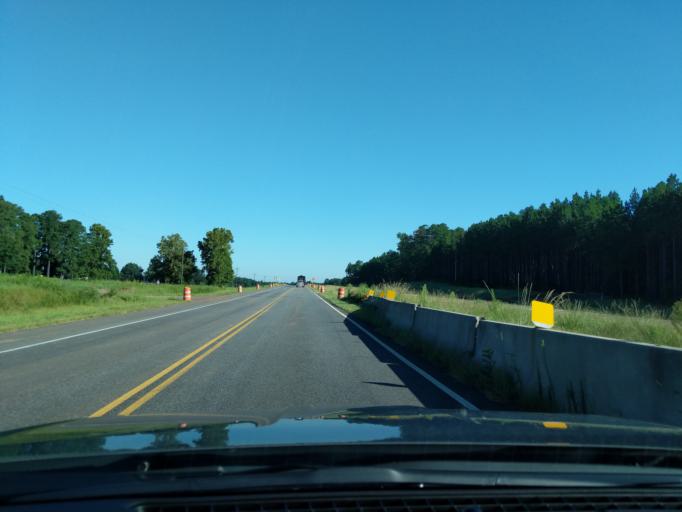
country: US
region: Georgia
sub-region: McDuffie County
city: Thomson
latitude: 33.5645
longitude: -82.5167
